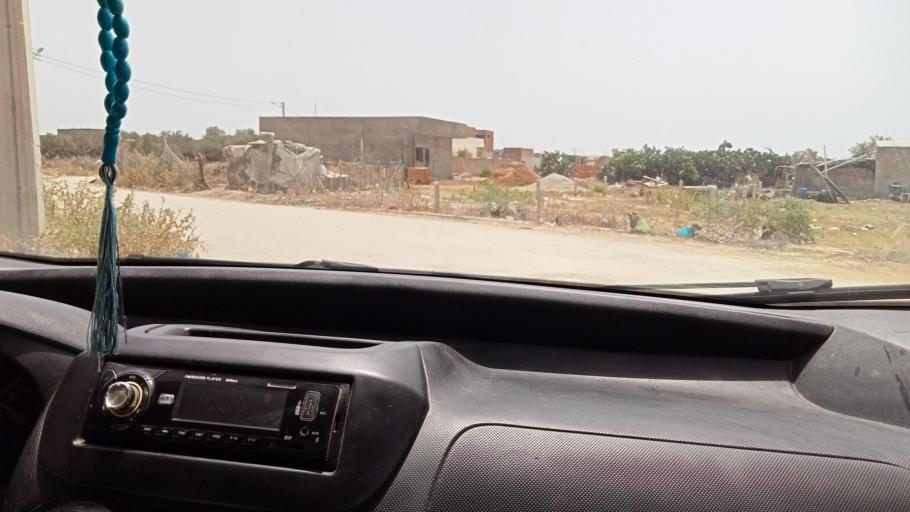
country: TN
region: Nabul
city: Qulaybiyah
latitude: 36.8609
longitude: 11.0832
